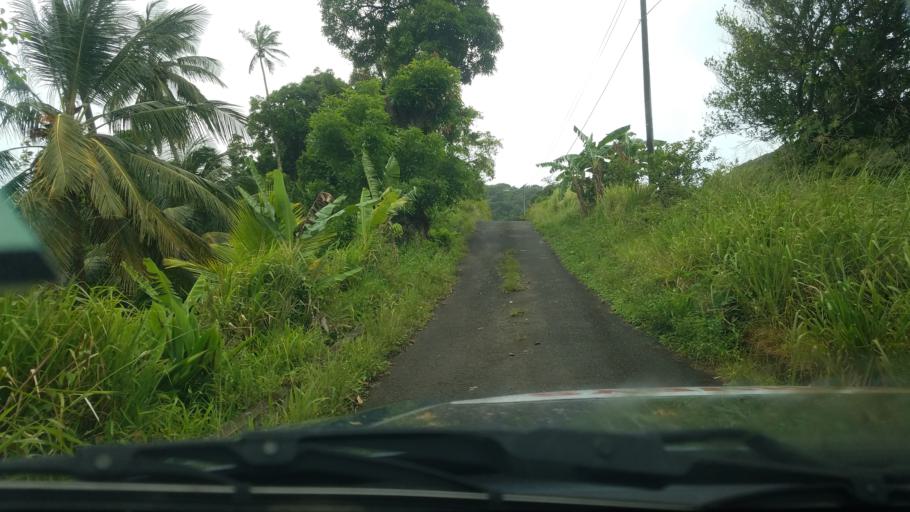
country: LC
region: Anse-la-Raye
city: Anse La Raye
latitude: 13.9237
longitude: -60.9950
